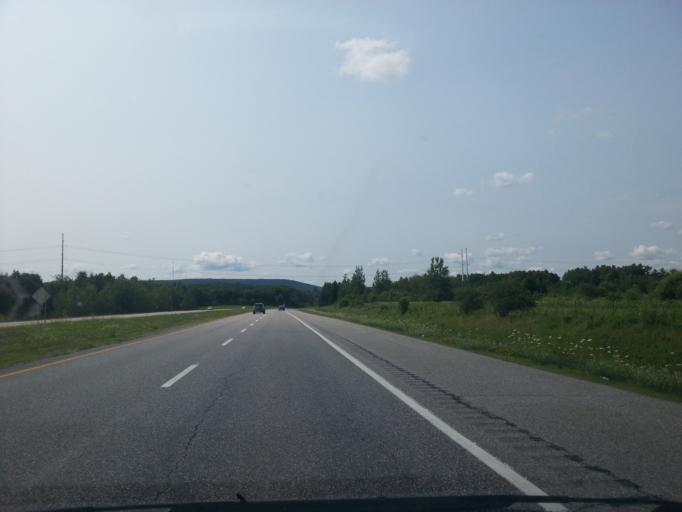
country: CA
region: Quebec
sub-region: Outaouais
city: Gatineau
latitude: 45.4805
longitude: -75.7889
